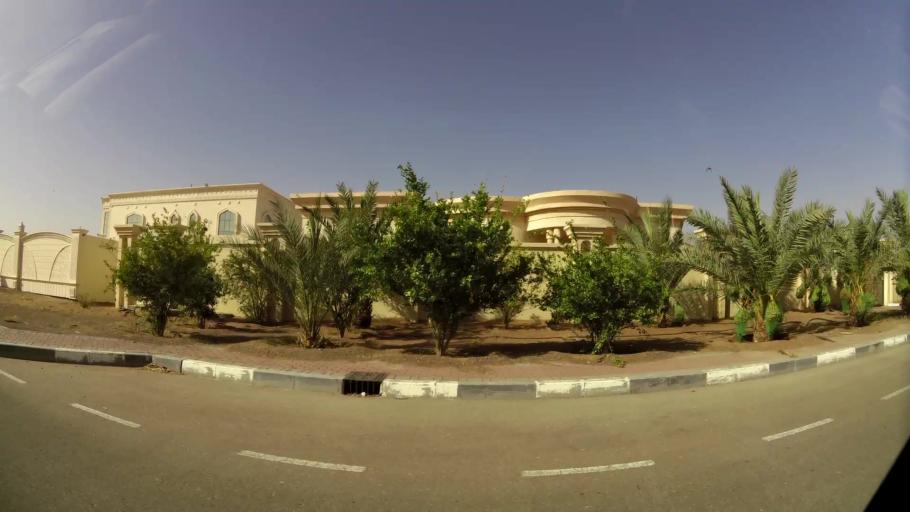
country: OM
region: Al Buraimi
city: Al Buraymi
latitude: 24.3485
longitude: 55.7989
